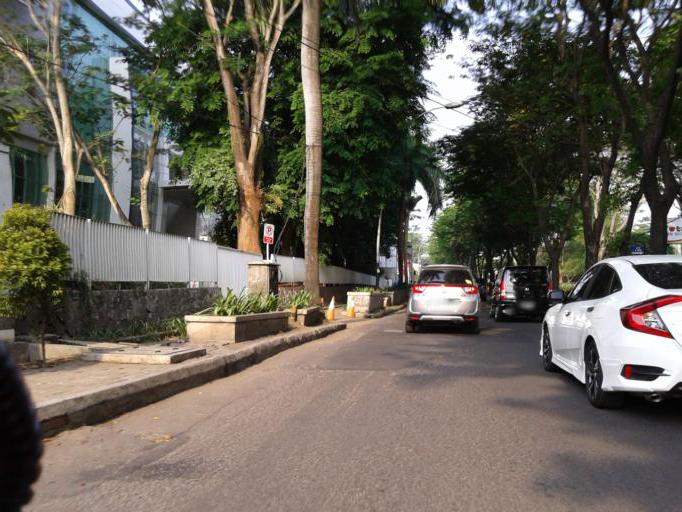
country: ID
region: Banten
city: South Tangerang
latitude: -6.2804
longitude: 106.7147
